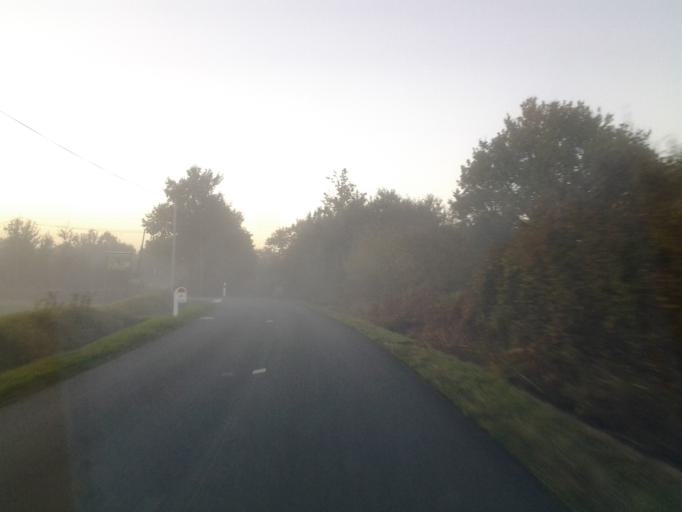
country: FR
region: Pays de la Loire
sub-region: Departement de la Vendee
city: Chateau-Guibert
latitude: 46.6406
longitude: -1.2330
